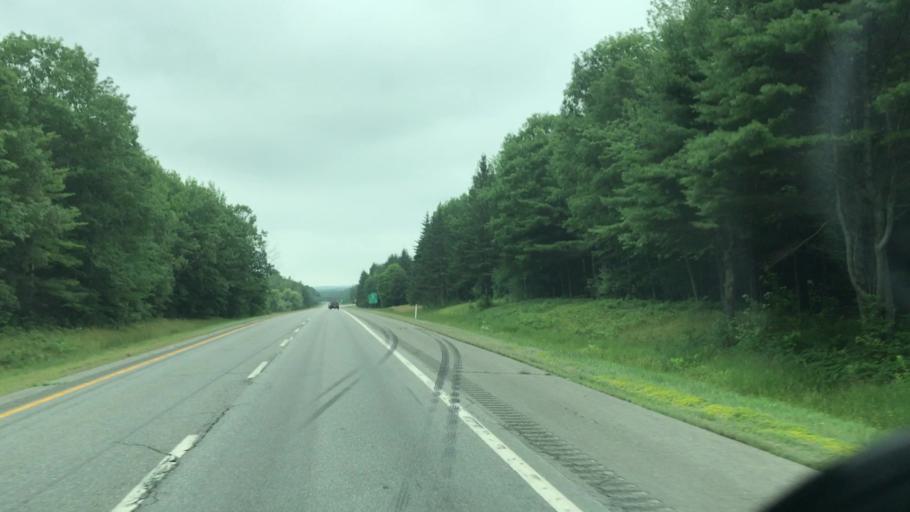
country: US
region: Maine
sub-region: Penobscot County
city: Milford
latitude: 44.9675
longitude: -68.7066
